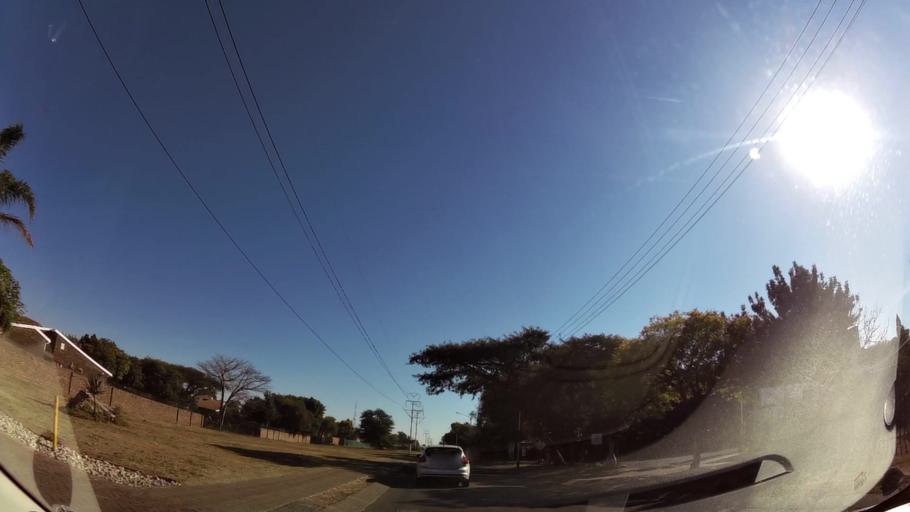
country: ZA
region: Gauteng
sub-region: City of Tshwane Metropolitan Municipality
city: Centurion
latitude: -25.8425
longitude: 28.2024
